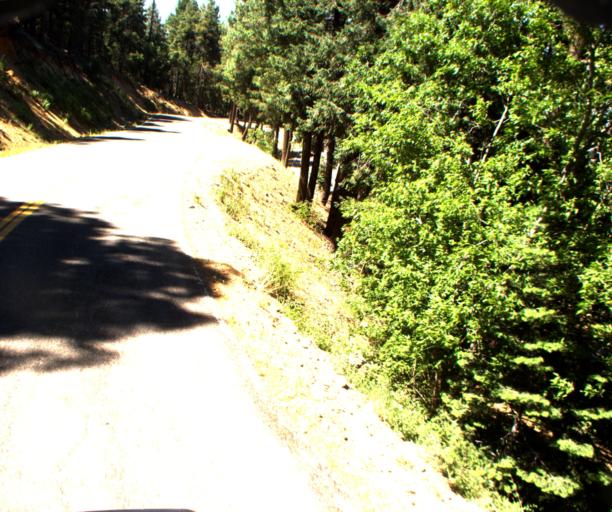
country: US
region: Arizona
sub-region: Graham County
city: Swift Trail Junction
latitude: 32.6300
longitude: -109.8249
